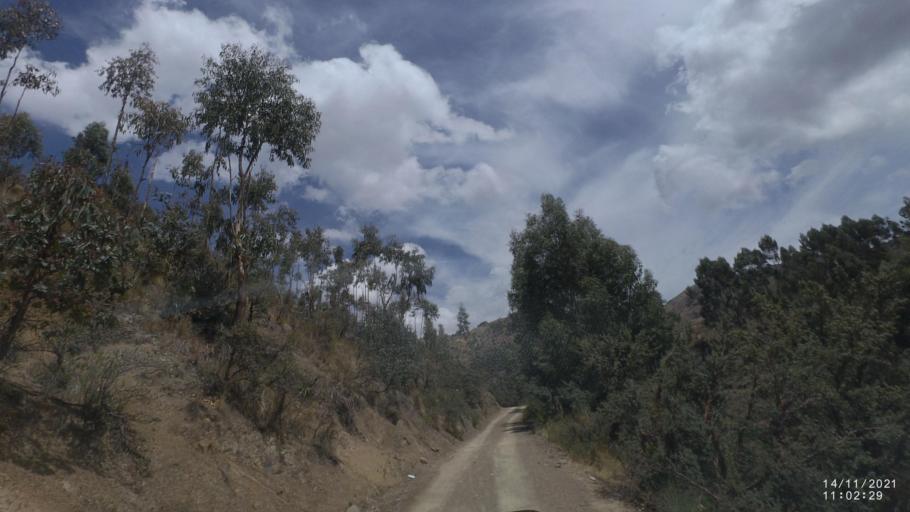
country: BO
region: Cochabamba
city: Cochabamba
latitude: -17.3391
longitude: -66.0584
